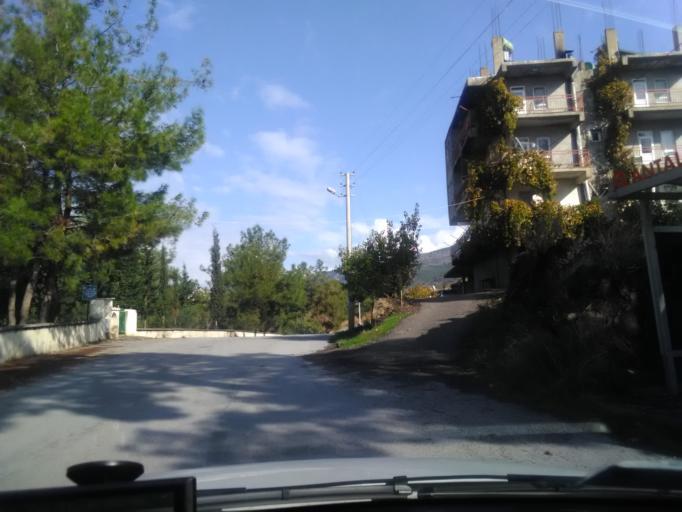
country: TR
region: Antalya
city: Gazipasa
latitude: 36.2888
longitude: 32.3247
